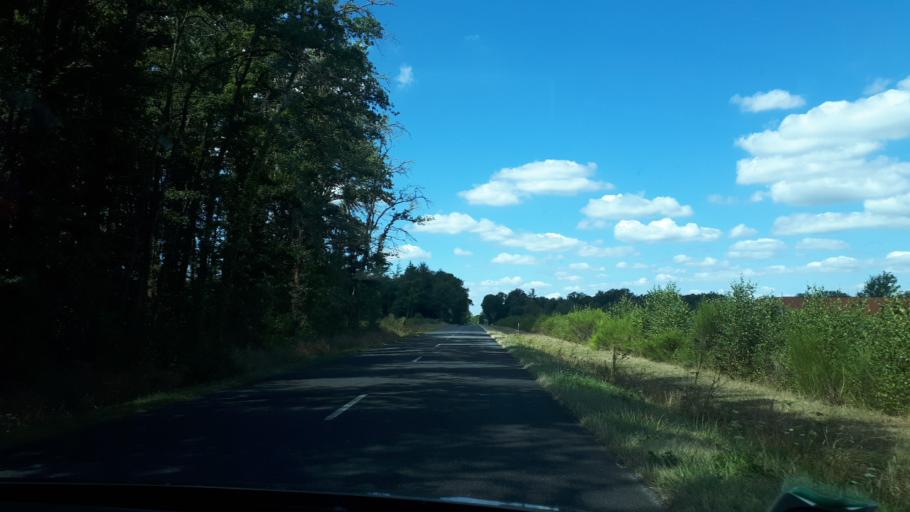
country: FR
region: Centre
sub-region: Departement du Loir-et-Cher
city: Neung-sur-Beuvron
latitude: 47.5346
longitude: 1.7687
